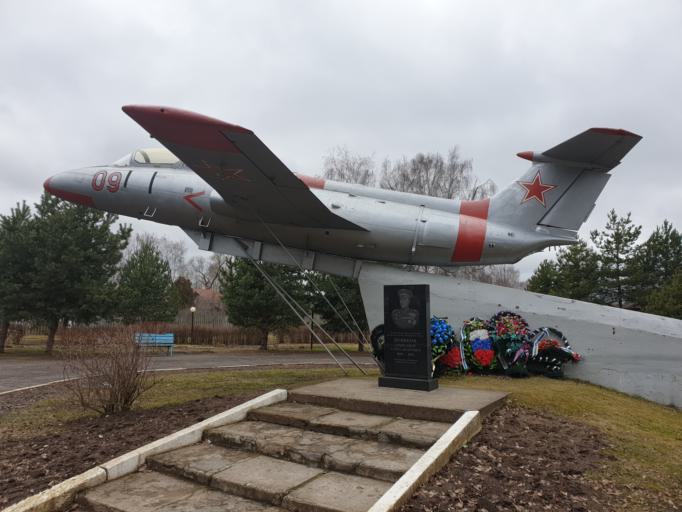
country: RU
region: Kostroma
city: Nerekhta
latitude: 57.4536
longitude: 40.5700
